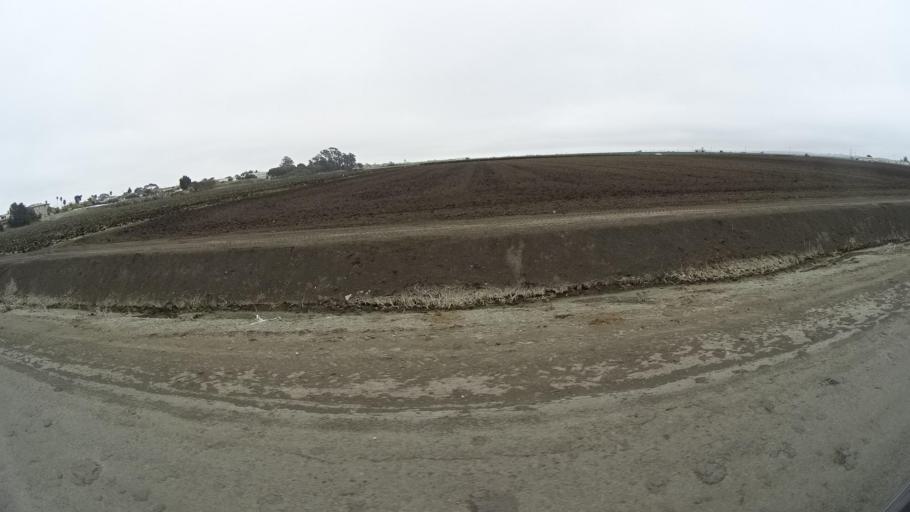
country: US
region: California
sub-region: Monterey County
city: Castroville
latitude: 36.7638
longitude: -121.7620
